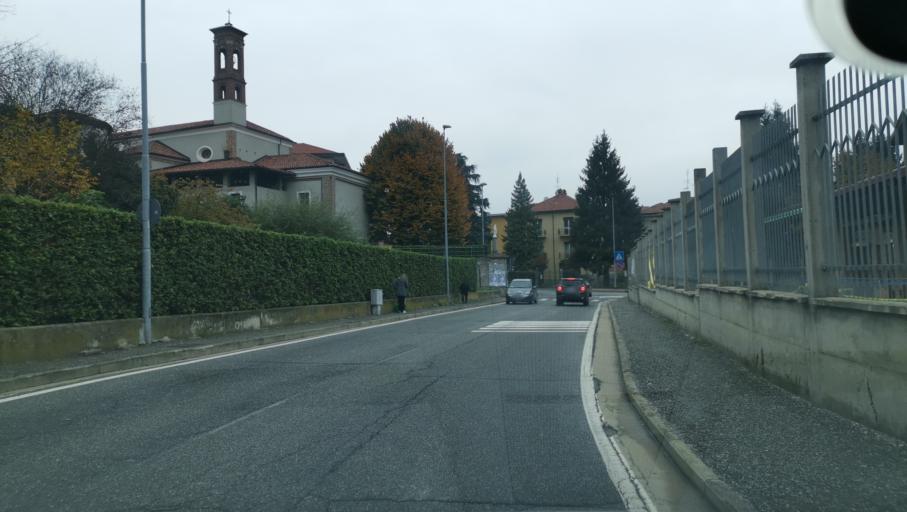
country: IT
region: Piedmont
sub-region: Provincia di Torino
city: Gassino Torinese
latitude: 45.1286
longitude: 7.8266
